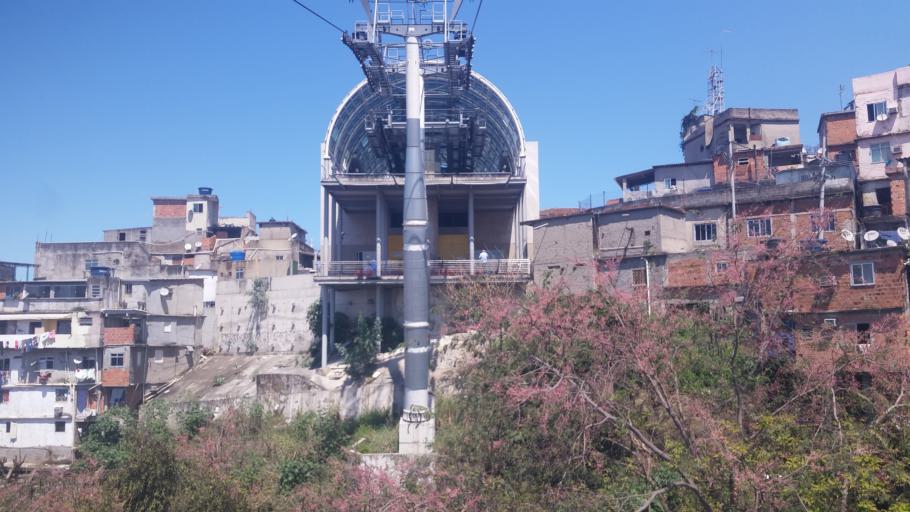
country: BR
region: Rio de Janeiro
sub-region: Rio De Janeiro
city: Rio de Janeiro
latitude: -22.8990
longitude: -43.1950
